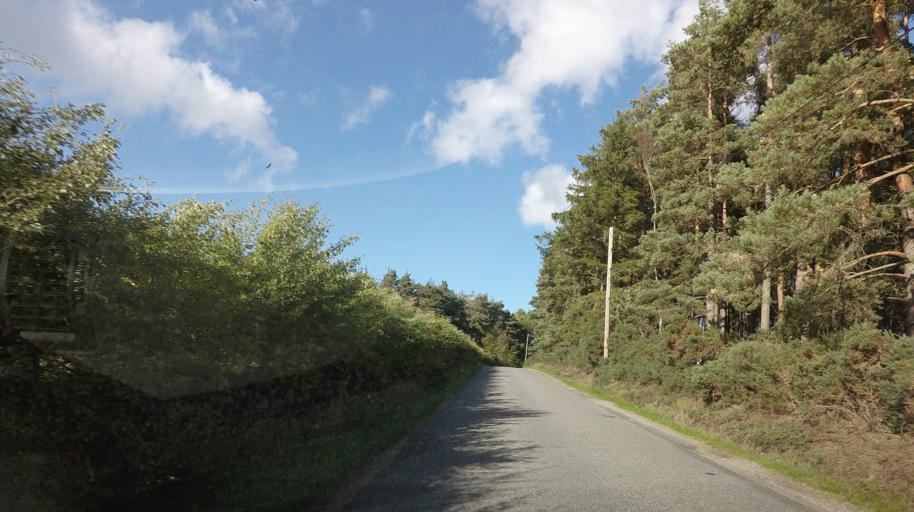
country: GB
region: Scotland
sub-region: Aberdeenshire
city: Banchory
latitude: 57.0730
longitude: -2.4640
